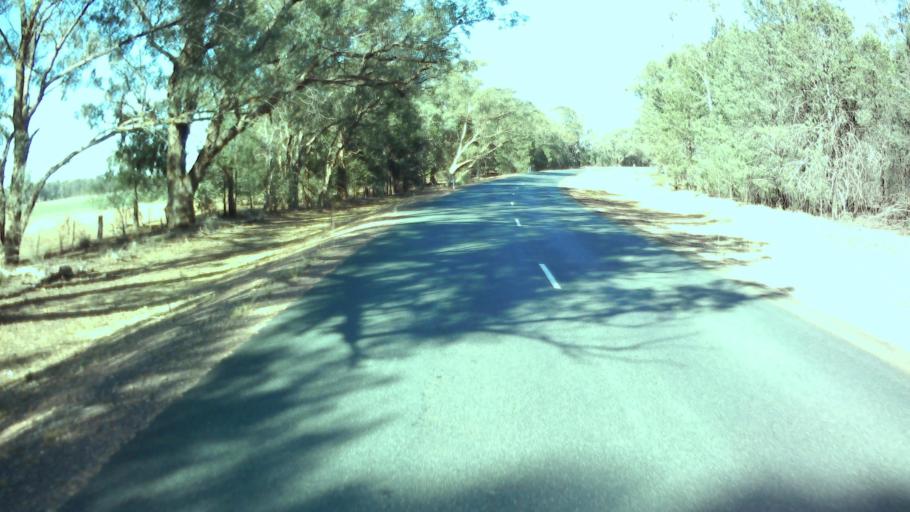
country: AU
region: New South Wales
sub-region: Weddin
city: Grenfell
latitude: -34.0349
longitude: 148.0858
